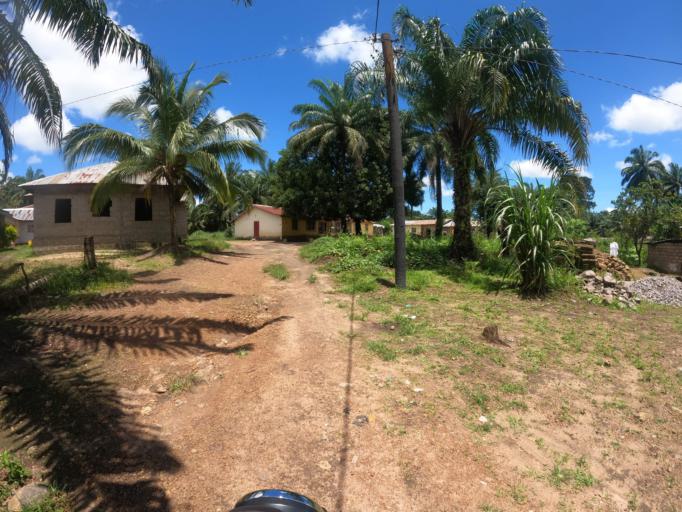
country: SL
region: Northern Province
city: Makeni
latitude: 8.8971
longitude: -12.0607
